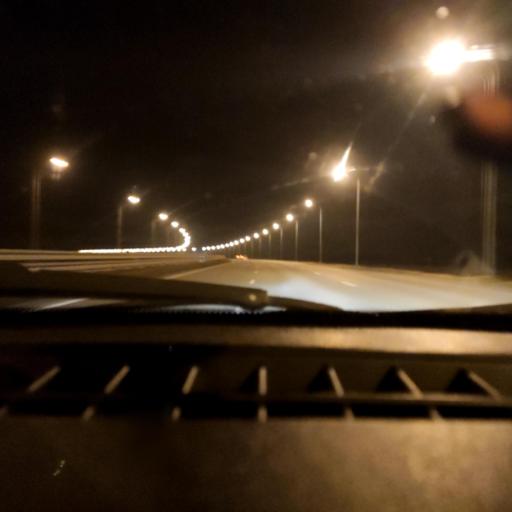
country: RU
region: Bashkortostan
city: Asanovo
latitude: 54.8954
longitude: 55.6394
